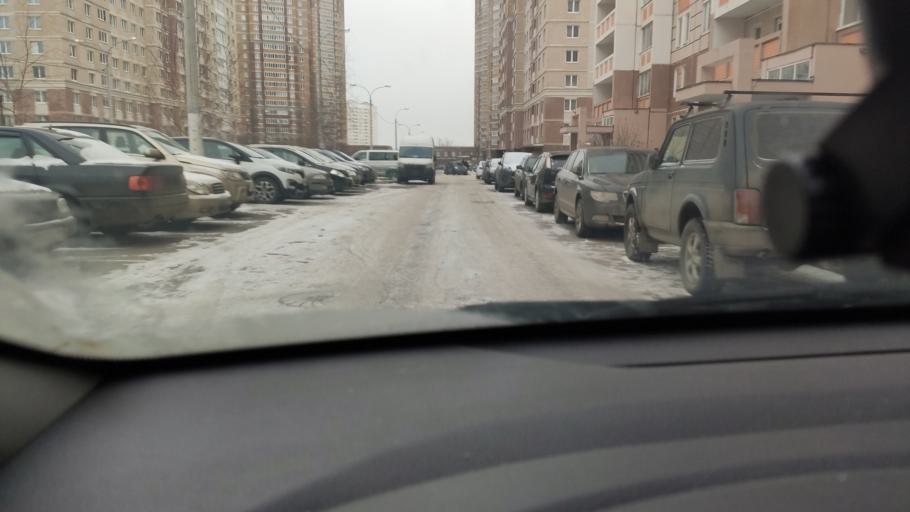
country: RU
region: Moskovskaya
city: Dubrovitsy
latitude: 55.4183
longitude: 37.4861
